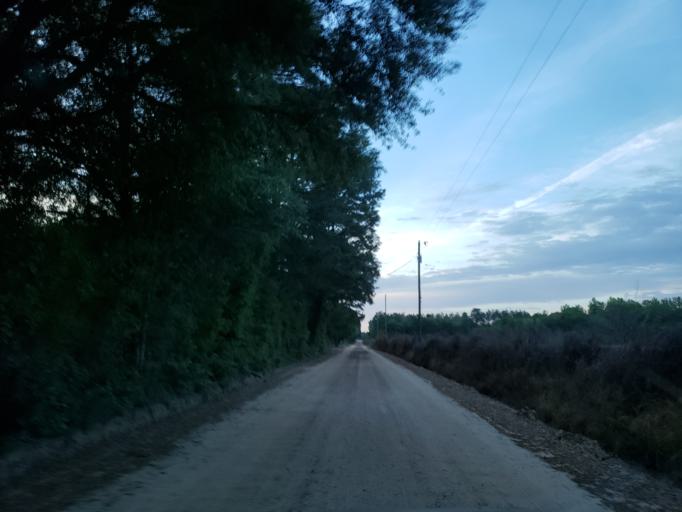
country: US
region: Georgia
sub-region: Lowndes County
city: Hahira
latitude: 30.9696
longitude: -83.3946
